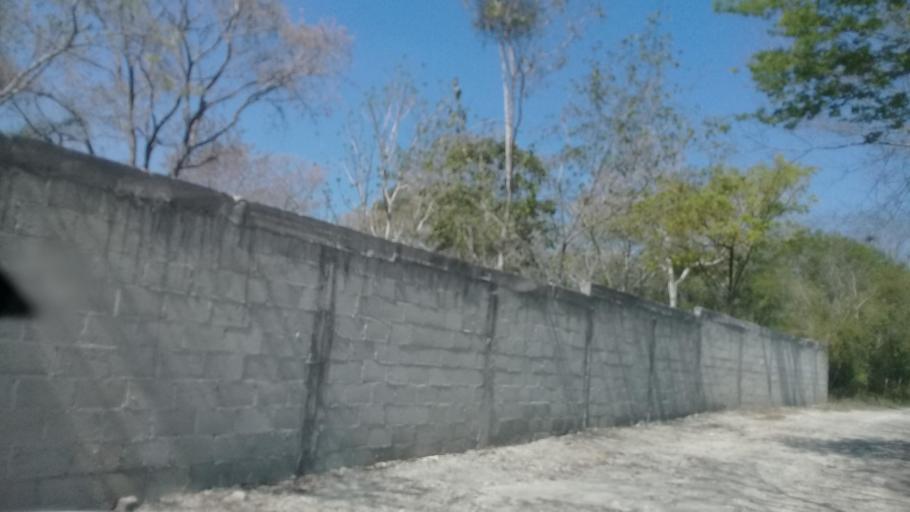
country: MX
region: Veracruz
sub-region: Emiliano Zapata
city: Plan del Rio
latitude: 19.3985
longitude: -96.6185
